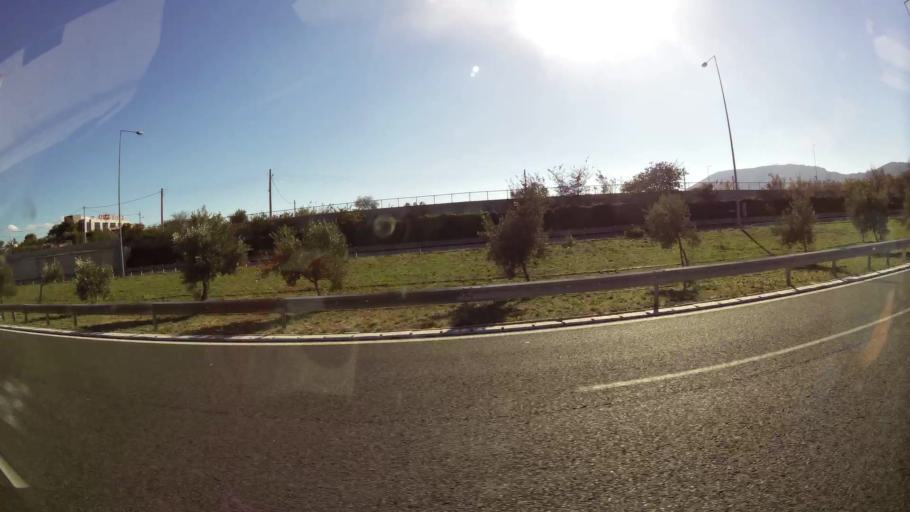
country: GR
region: Attica
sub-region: Nomarchia Anatolikis Attikis
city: Pallini
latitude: 37.9953
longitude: 23.8820
